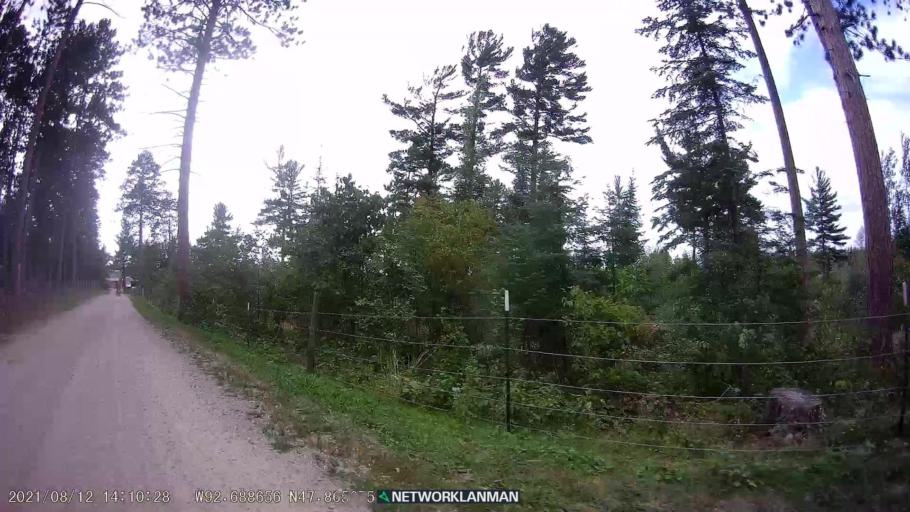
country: US
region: Minnesota
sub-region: Saint Louis County
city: Mountain Iron
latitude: 47.8654
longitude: -92.6889
